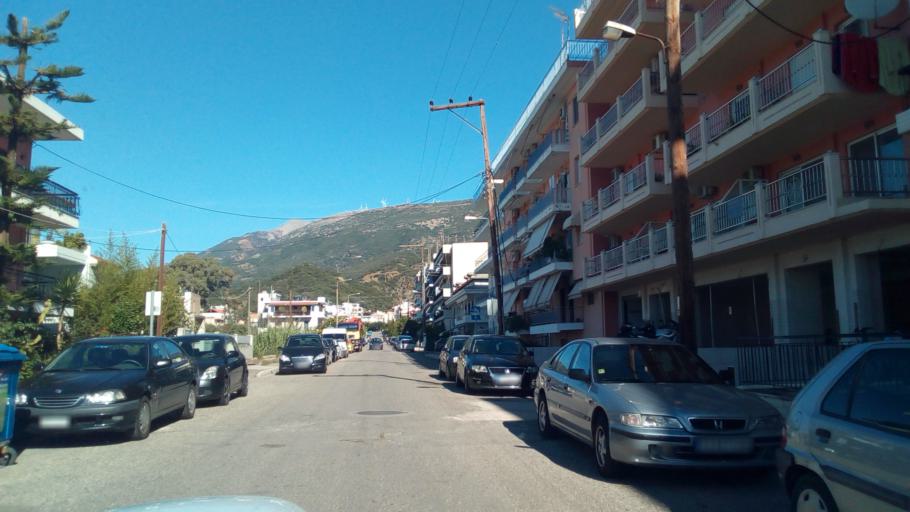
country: GR
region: West Greece
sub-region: Nomos Aitolias kai Akarnanias
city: Nafpaktos
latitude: 38.3884
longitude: 21.8211
